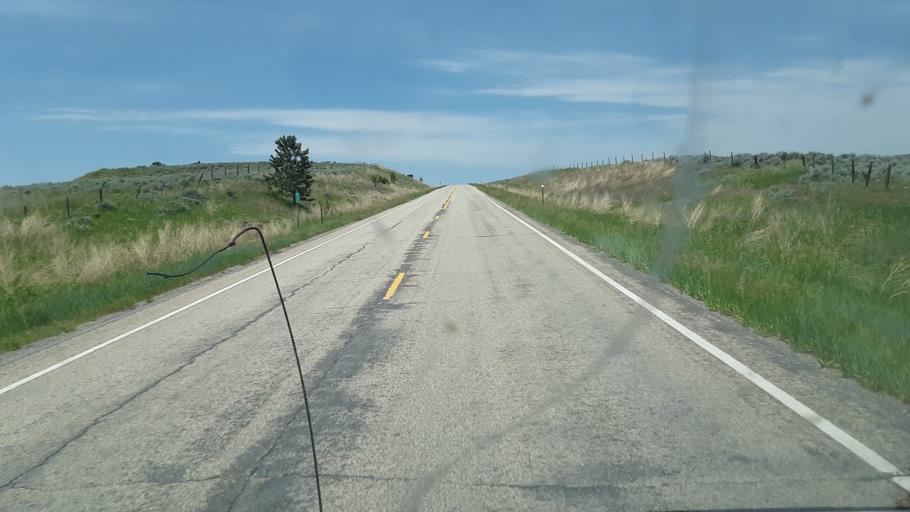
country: US
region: Montana
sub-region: Stillwater County
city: Columbus
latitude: 45.4798
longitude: -109.0101
